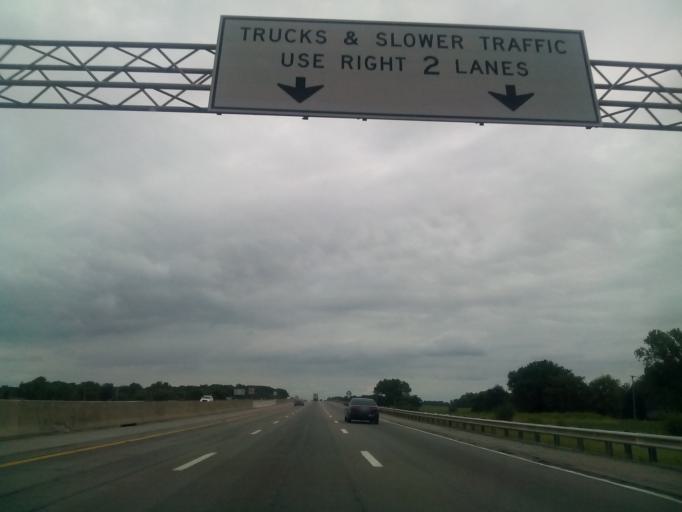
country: US
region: Ohio
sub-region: Huron County
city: Monroeville
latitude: 41.3393
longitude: -82.7524
